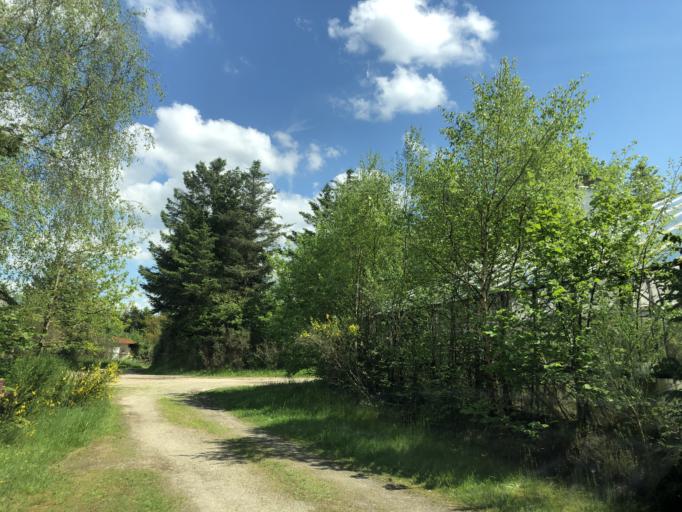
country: DK
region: Central Jutland
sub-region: Holstebro Kommune
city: Ulfborg
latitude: 56.2412
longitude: 8.4277
